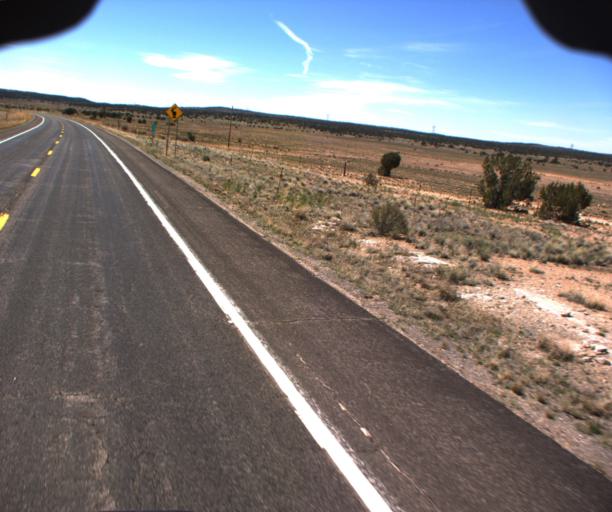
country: US
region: Arizona
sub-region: Mohave County
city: Peach Springs
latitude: 35.5539
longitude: -113.3210
